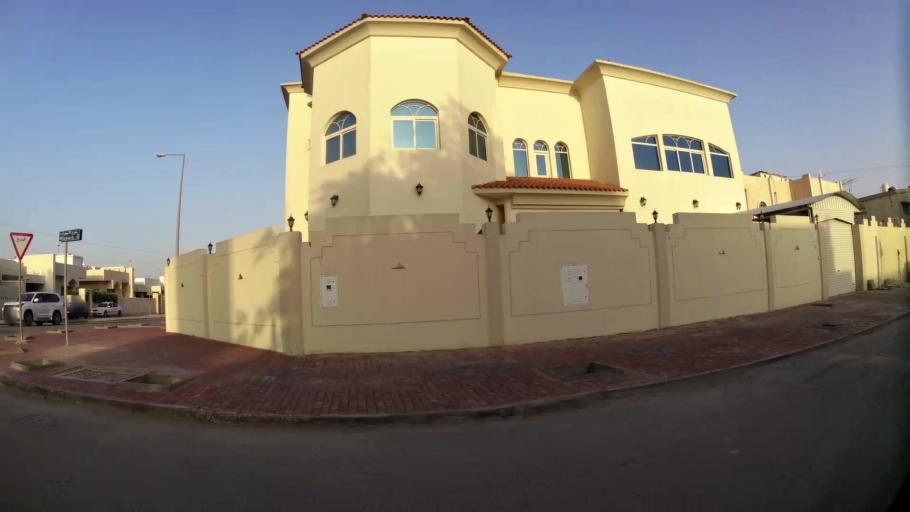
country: QA
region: Baladiyat ar Rayyan
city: Ar Rayyan
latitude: 25.3187
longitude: 51.4565
